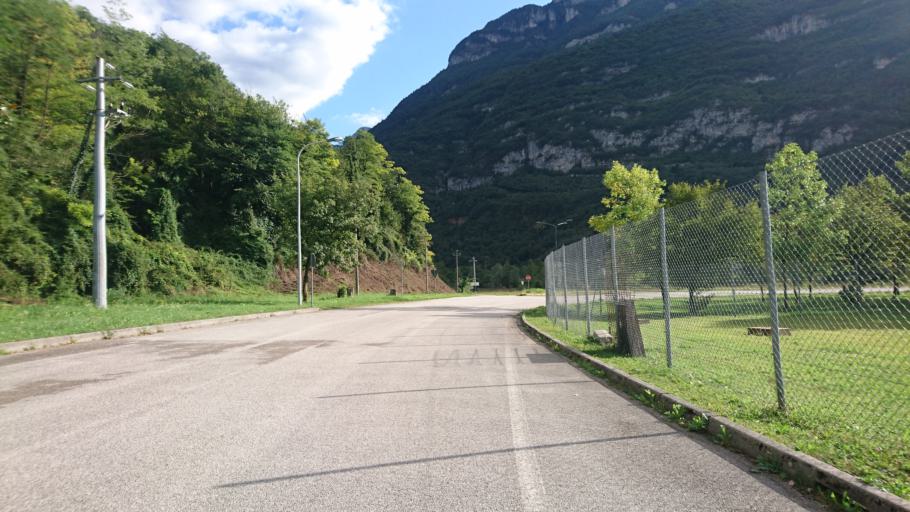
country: IT
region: Veneto
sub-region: Provincia di Belluno
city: Castello Lavazzo
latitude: 46.2772
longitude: 12.3026
